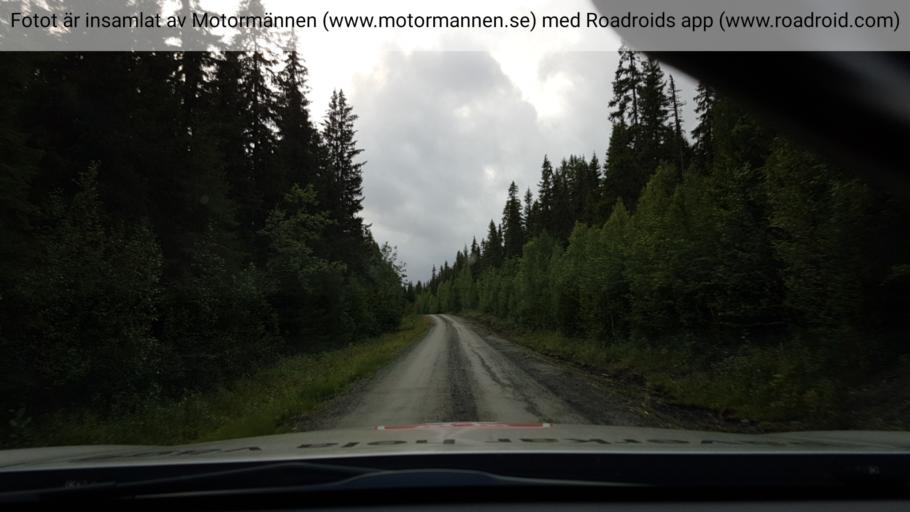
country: SE
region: Vaesterbotten
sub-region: Vilhelmina Kommun
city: Sjoberg
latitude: 65.4993
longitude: 15.5736
